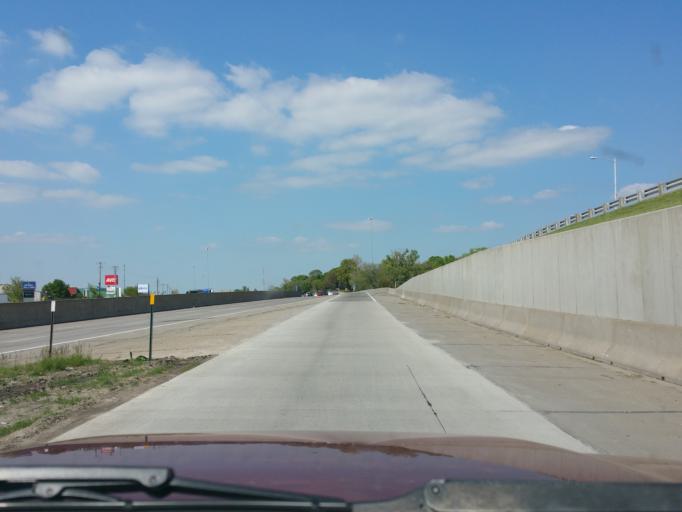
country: US
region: Kansas
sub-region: Johnson County
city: Overland Park
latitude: 38.9947
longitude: -94.6962
